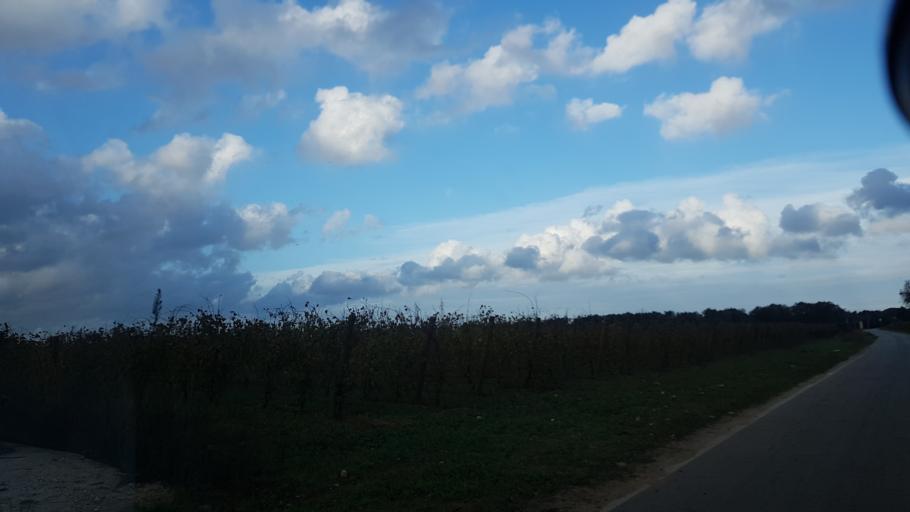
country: IT
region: Apulia
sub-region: Provincia di Brindisi
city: San Pietro Vernotico
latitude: 40.5076
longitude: 18.0186
